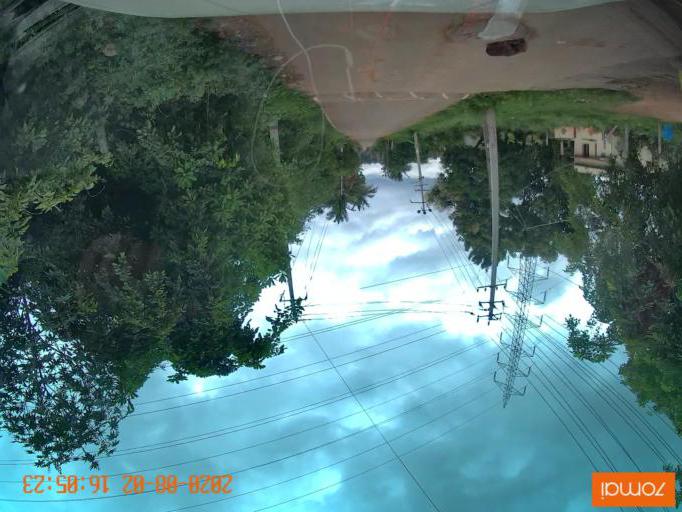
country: IN
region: Karnataka
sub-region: Bangalore Urban
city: Anekal
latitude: 12.8333
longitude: 77.6392
